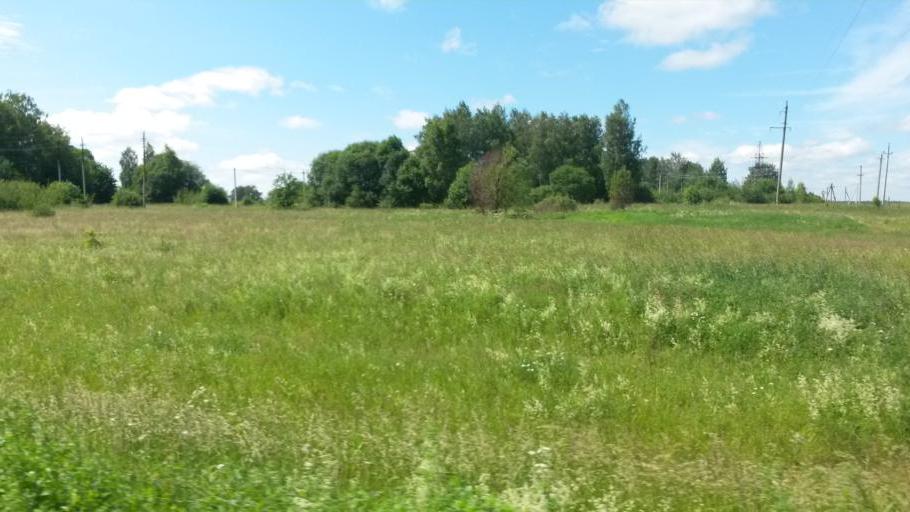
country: RU
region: Jaroslavl
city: Dubki
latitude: 57.2995
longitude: 40.1828
